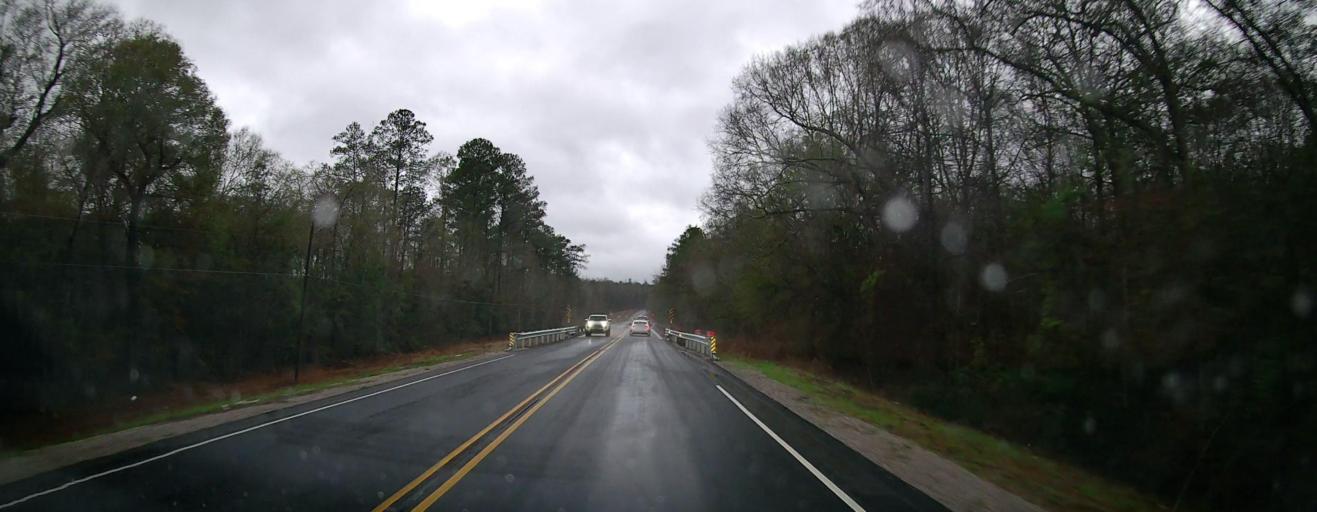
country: US
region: Alabama
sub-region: Chilton County
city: Clanton
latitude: 32.6156
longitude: -86.7276
